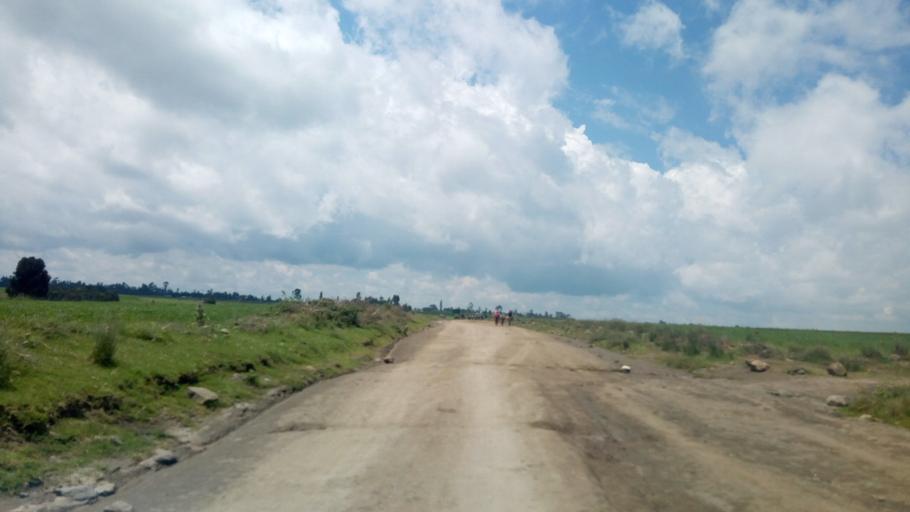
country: ET
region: Oromiya
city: Sendafa
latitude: 8.9846
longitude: 39.1253
